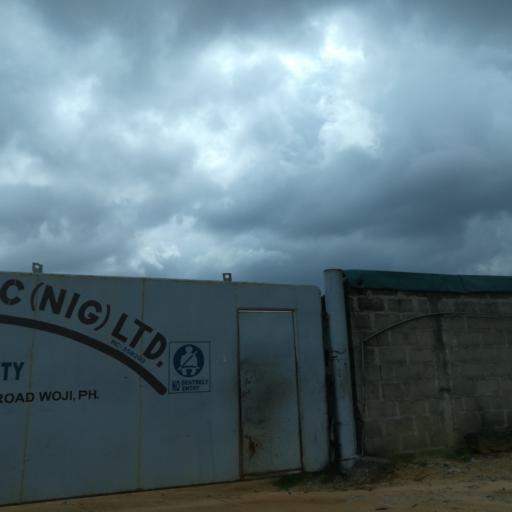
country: NG
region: Rivers
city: Port Harcourt
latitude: 4.8104
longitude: 7.0599
